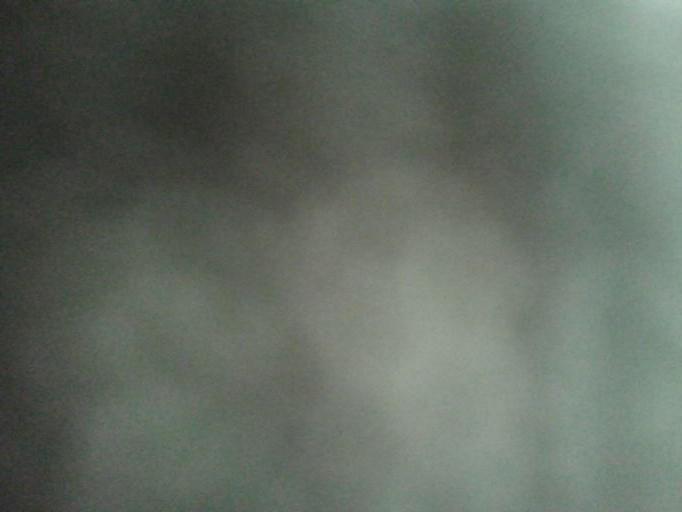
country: BR
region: Maranhao
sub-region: Sao Luis
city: Sao Luis
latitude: -2.6906
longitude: -44.3017
